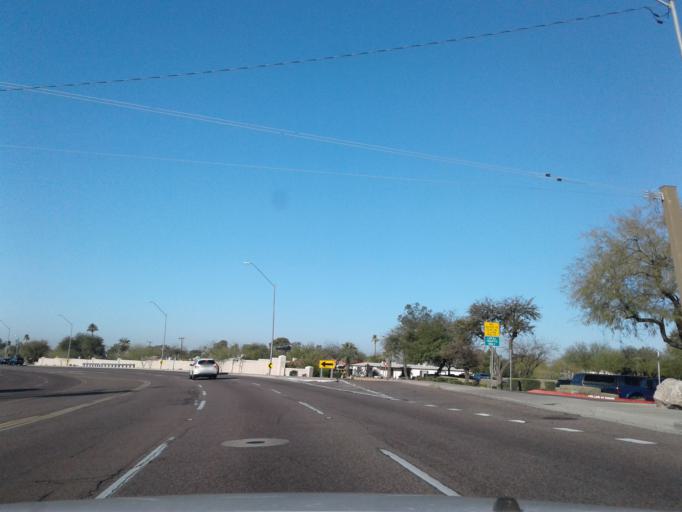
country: US
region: Arizona
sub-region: Maricopa County
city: Paradise Valley
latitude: 33.5557
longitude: -112.0460
